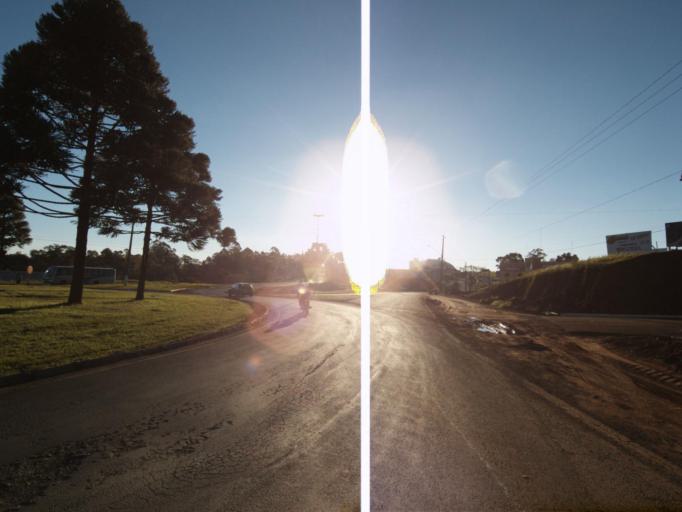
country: BR
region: Santa Catarina
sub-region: Chapeco
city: Chapeco
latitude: -26.8372
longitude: -52.9868
